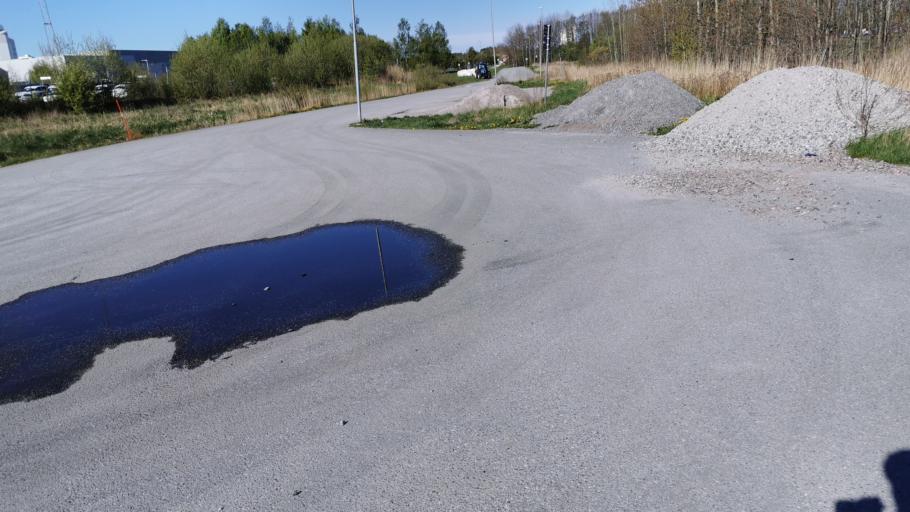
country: SE
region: OErebro
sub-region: Orebro Kommun
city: Orebro
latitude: 59.2997
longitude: 15.2110
